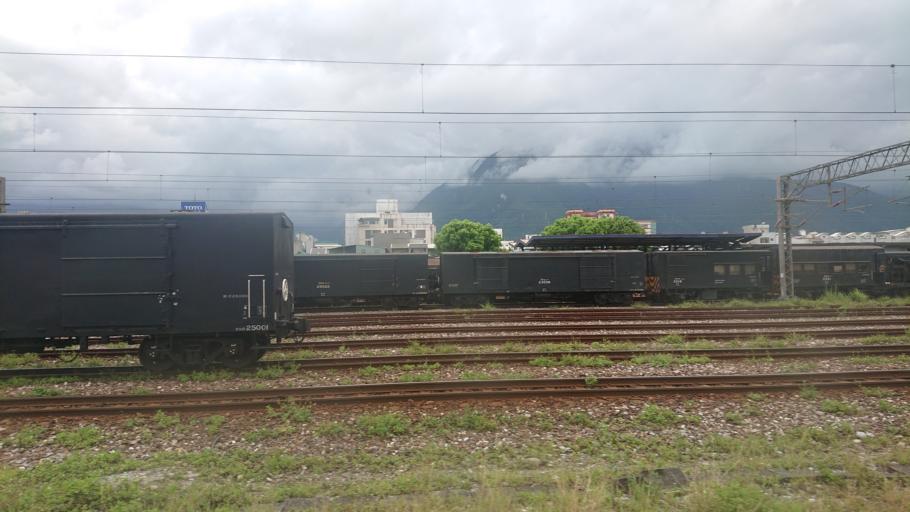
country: TW
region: Taiwan
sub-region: Hualien
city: Hualian
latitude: 23.9948
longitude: 121.6018
